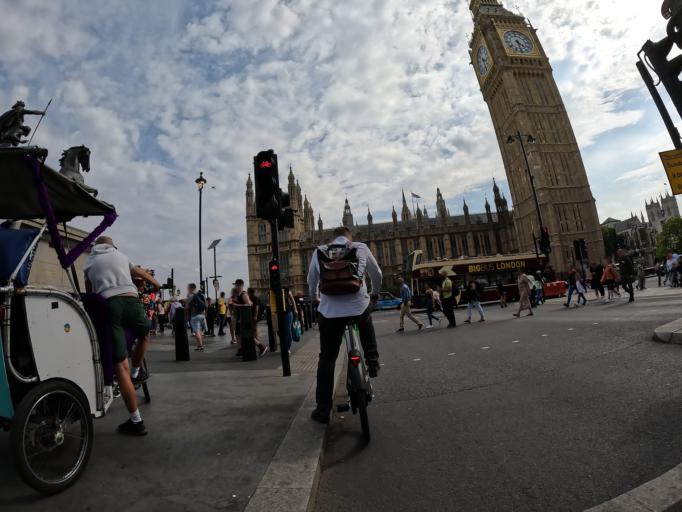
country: GB
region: England
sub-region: Greater London
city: Orpington
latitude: 51.3518
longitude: 0.1059
